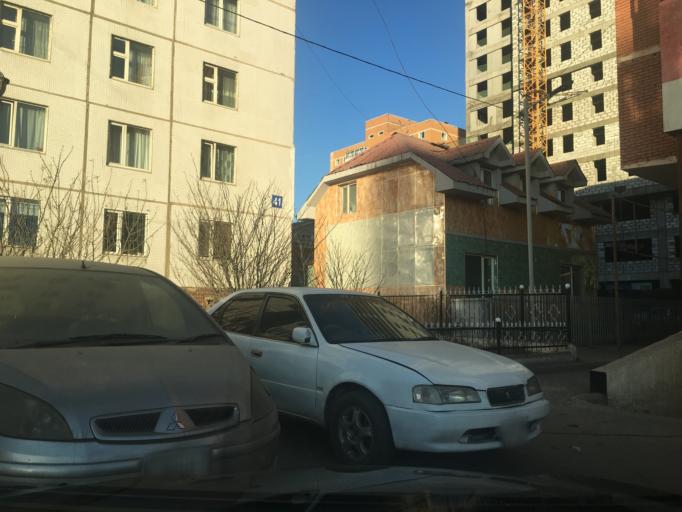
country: MN
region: Ulaanbaatar
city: Ulaanbaatar
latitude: 47.9187
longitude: 106.8863
